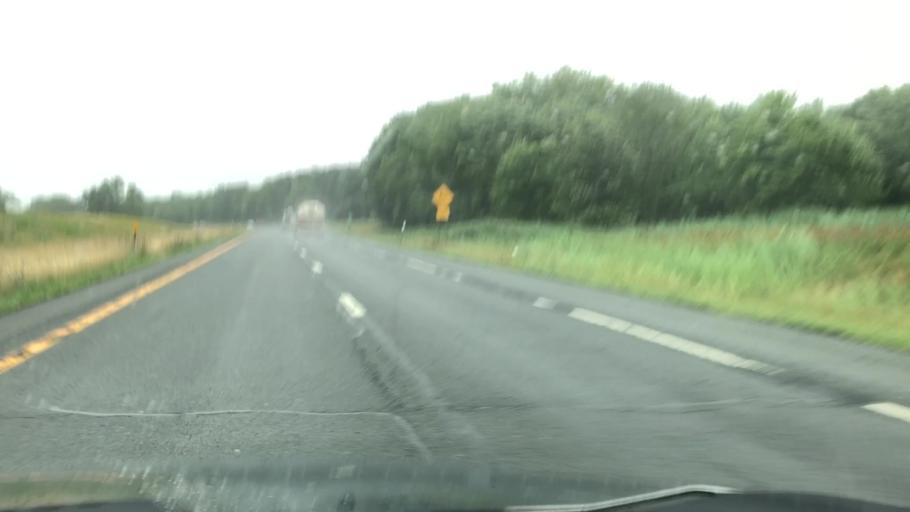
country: US
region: New York
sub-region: Orange County
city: Otisville
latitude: 41.3973
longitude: -74.5399
